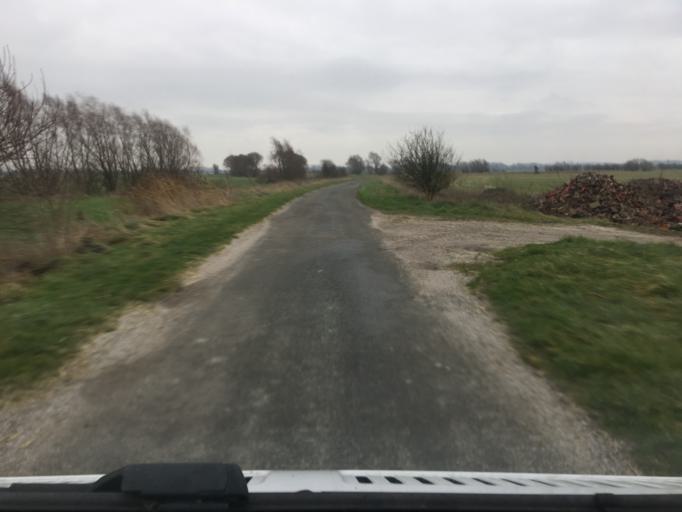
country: FR
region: Picardie
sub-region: Departement de la Somme
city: Pende
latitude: 50.1908
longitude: 1.5469
